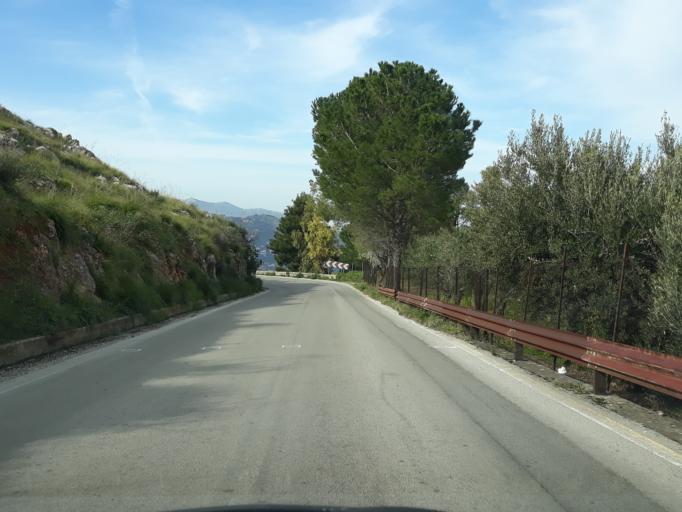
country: IT
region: Sicily
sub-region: Palermo
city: Piano Maglio-Blandino
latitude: 38.0433
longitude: 13.3101
